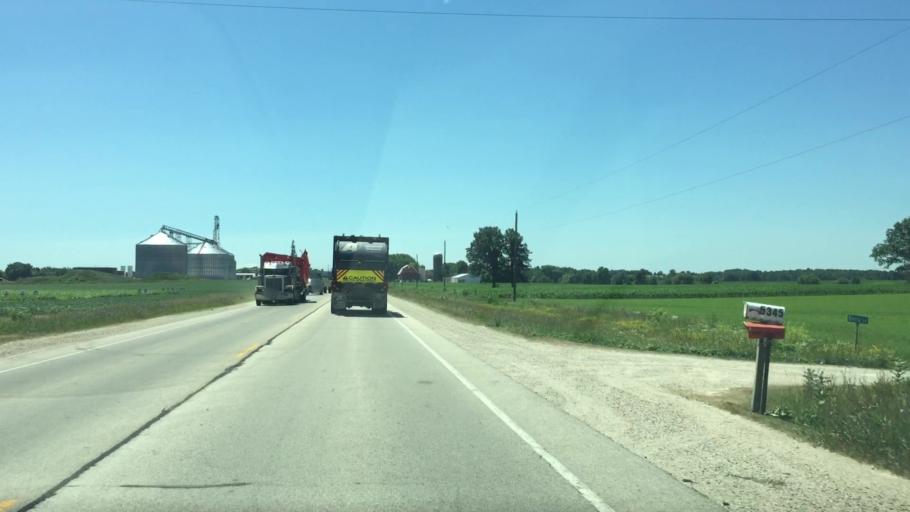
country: US
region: Wisconsin
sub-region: Calumet County
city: Chilton
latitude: 44.0822
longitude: -88.1635
